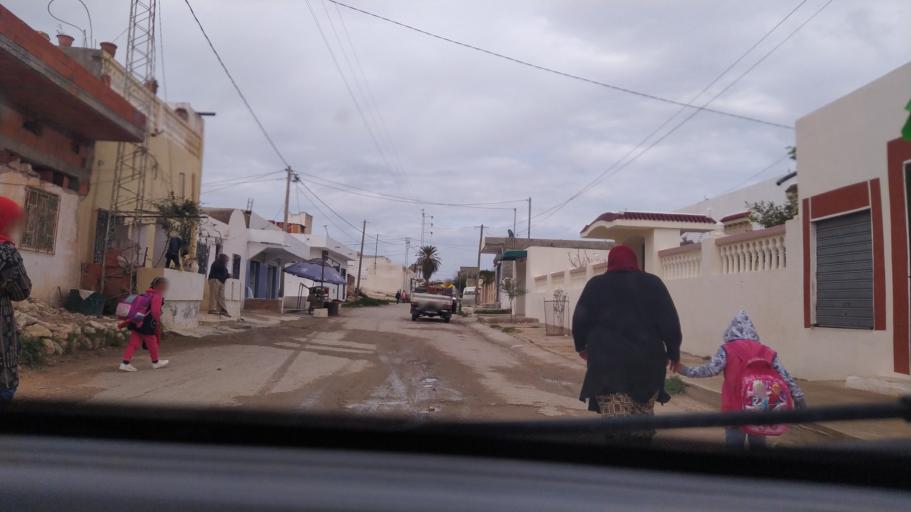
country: TN
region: Al Munastir
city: Sidi Bin Nur
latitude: 35.5249
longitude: 10.9372
